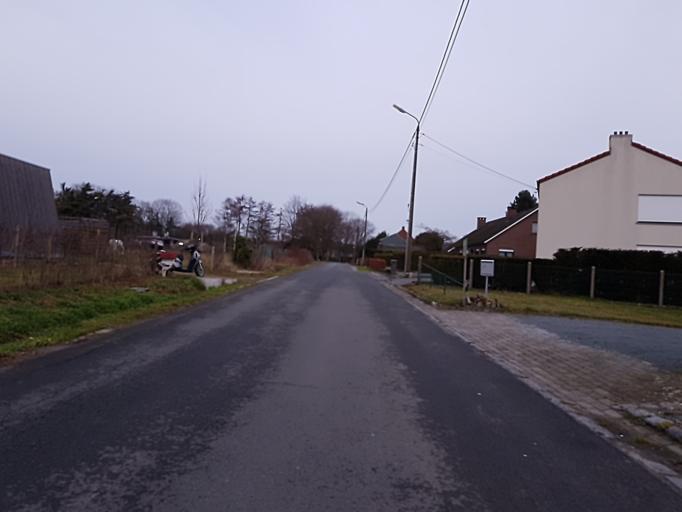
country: BE
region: Flanders
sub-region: Provincie Antwerpen
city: Putte
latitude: 51.0500
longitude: 4.6610
